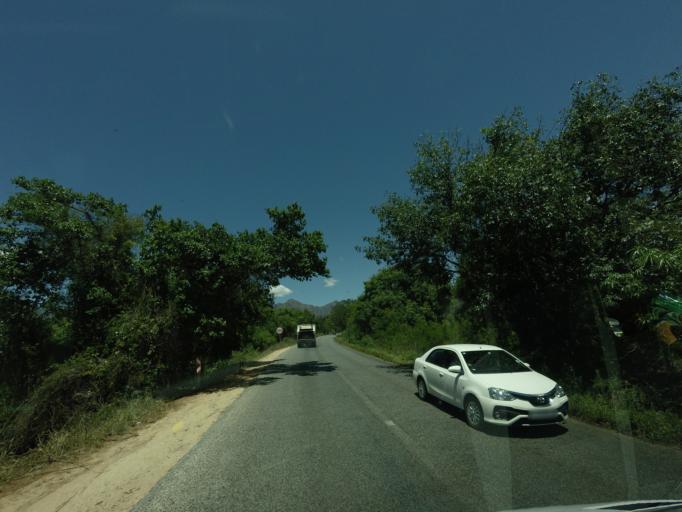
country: ZA
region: Limpopo
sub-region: Mopani District Municipality
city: Hoedspruit
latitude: -24.4069
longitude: 30.7958
